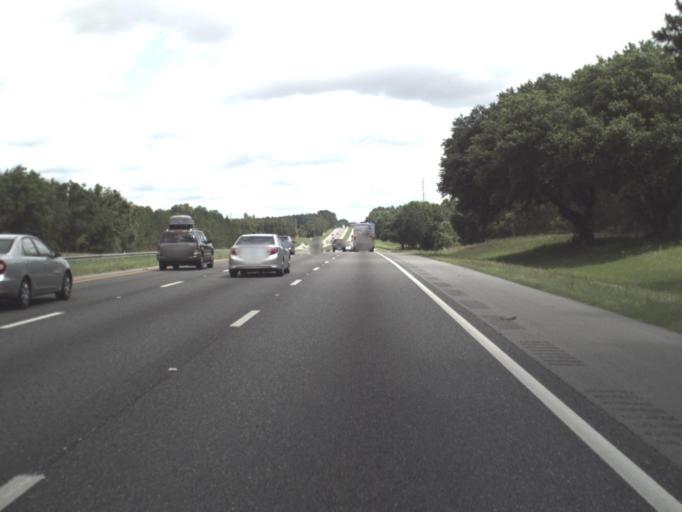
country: US
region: Florida
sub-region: Columbia County
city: Watertown
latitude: 30.0142
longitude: -82.6071
